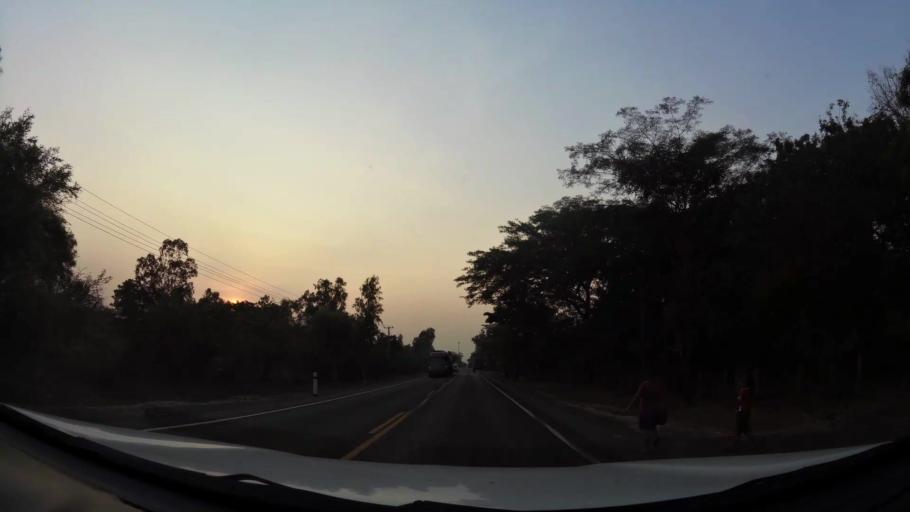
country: NI
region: Leon
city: La Paz Centro
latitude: 12.3301
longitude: -86.8051
